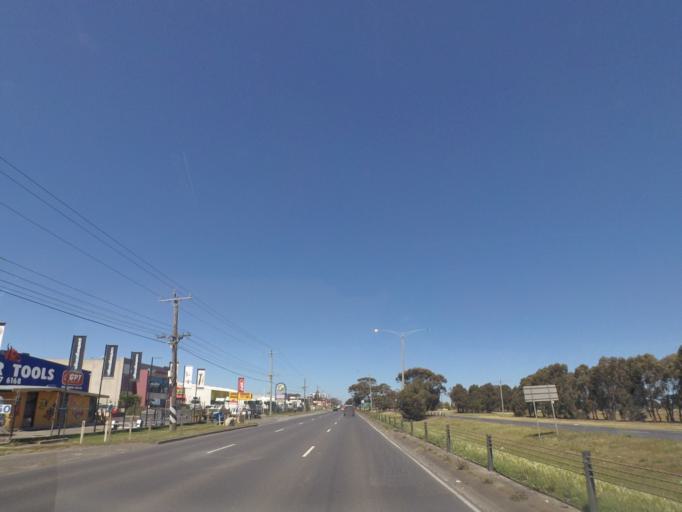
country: AU
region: Victoria
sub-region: Hume
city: Campbellfield
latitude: -37.6637
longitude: 144.9547
